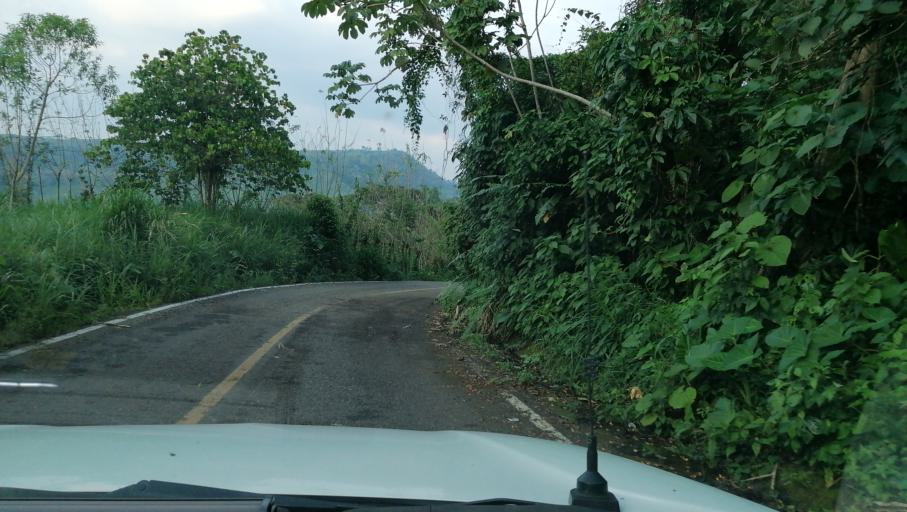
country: MX
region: Chiapas
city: Pichucalco
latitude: 17.5110
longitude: -93.2091
